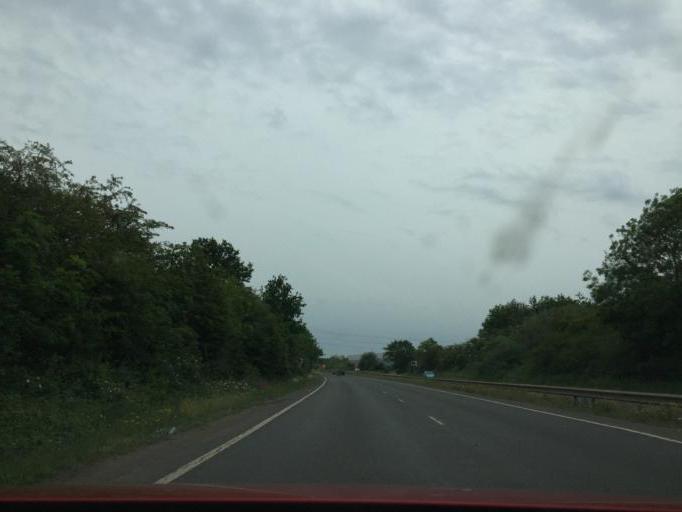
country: GB
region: England
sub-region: Warwickshire
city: Nuneaton
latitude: 52.5066
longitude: -1.4762
